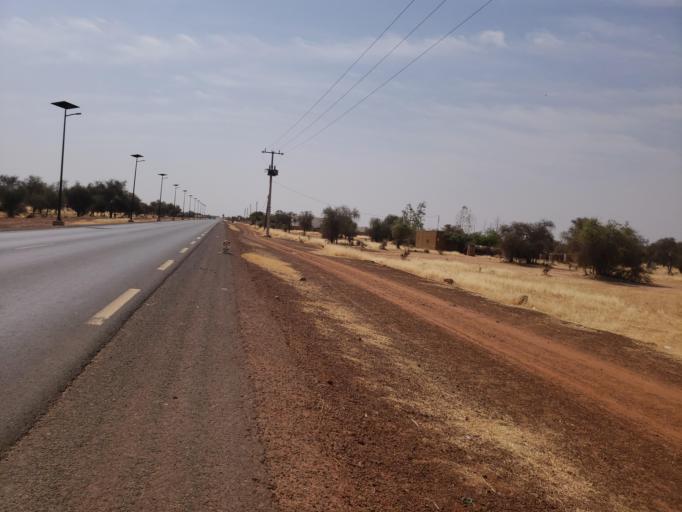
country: SN
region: Matam
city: Ranerou
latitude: 15.2909
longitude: -13.9625
